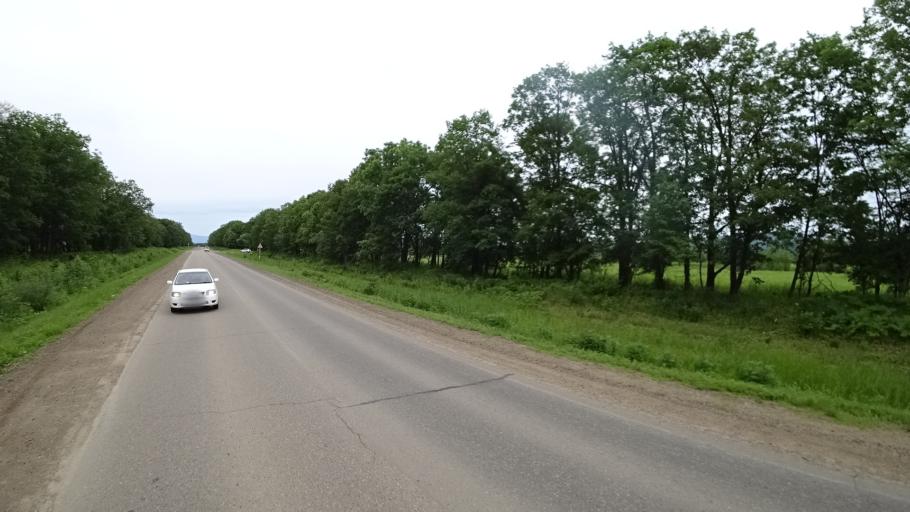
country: RU
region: Primorskiy
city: Novosysoyevka
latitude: 44.1902
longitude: 133.3545
